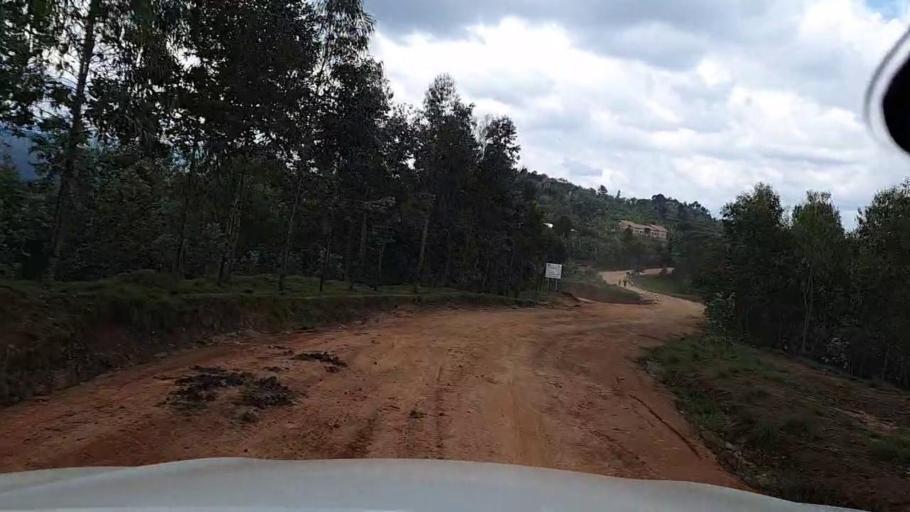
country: RW
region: Southern Province
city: Nzega
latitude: -2.7055
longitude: 29.5087
